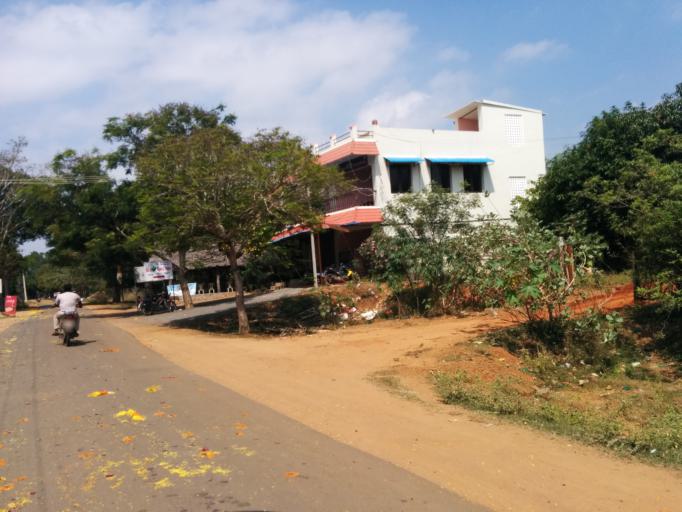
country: IN
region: Tamil Nadu
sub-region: Villupuram
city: Auroville
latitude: 11.9996
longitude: 79.8009
